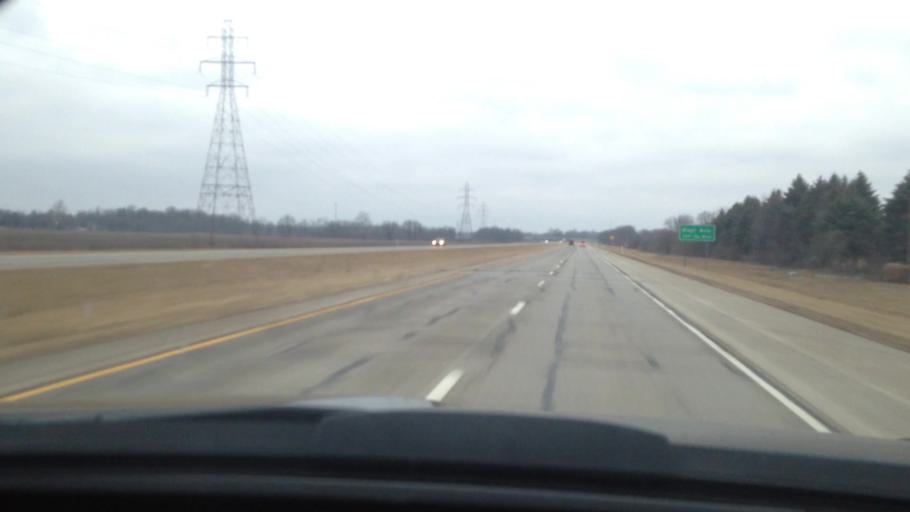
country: US
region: Indiana
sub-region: Delaware County
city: Muncie
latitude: 40.1421
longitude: -85.4145
